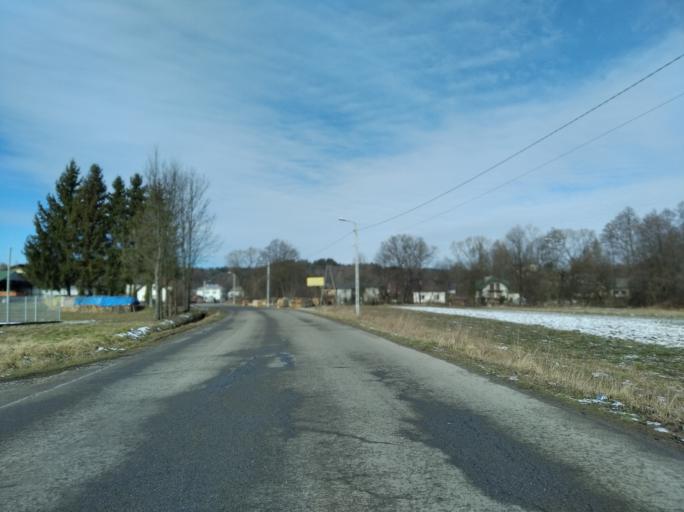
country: PL
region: Subcarpathian Voivodeship
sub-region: Powiat brzozowski
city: Jasienica Rosielna
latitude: 49.7524
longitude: 21.9137
